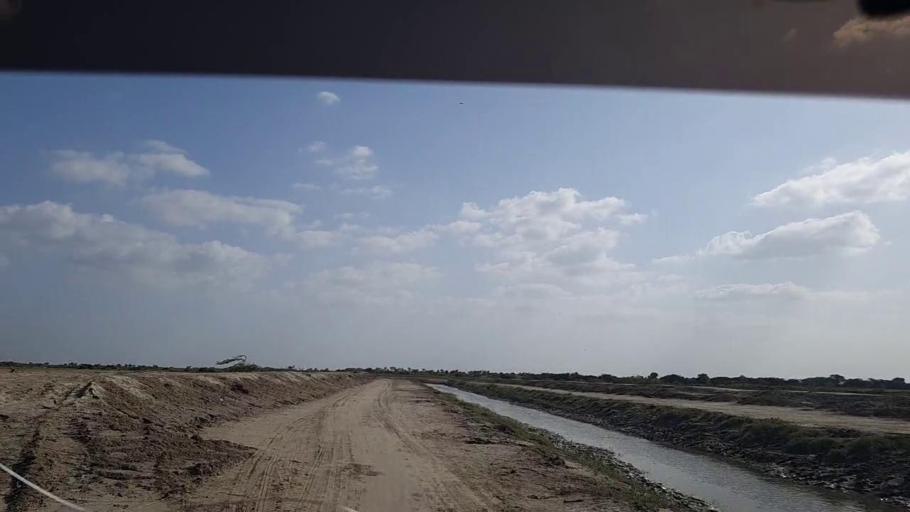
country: PK
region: Sindh
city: Kadhan
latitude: 24.4547
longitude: 68.8583
